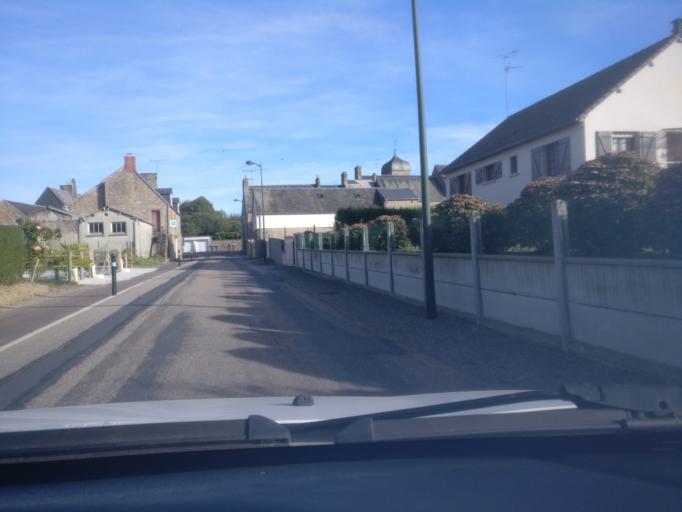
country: FR
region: Lower Normandy
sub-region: Departement de la Manche
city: Marcey-les-Greves
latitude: 48.7015
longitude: -1.4423
